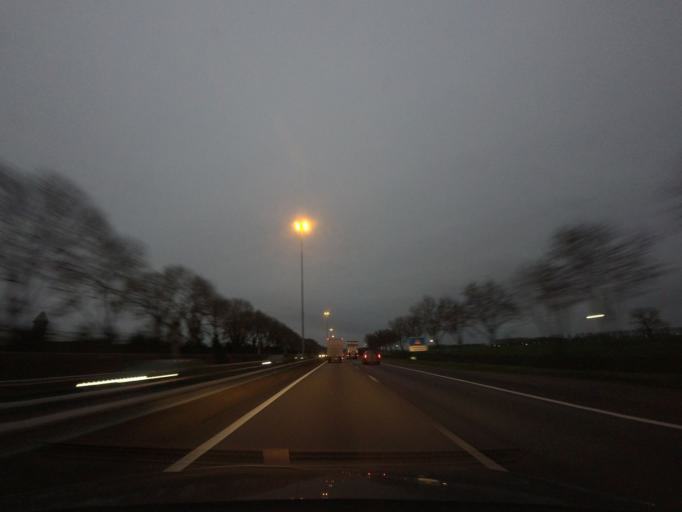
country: NL
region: Utrecht
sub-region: Gemeente Lopik
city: Lopik
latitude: 51.9229
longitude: 4.9907
